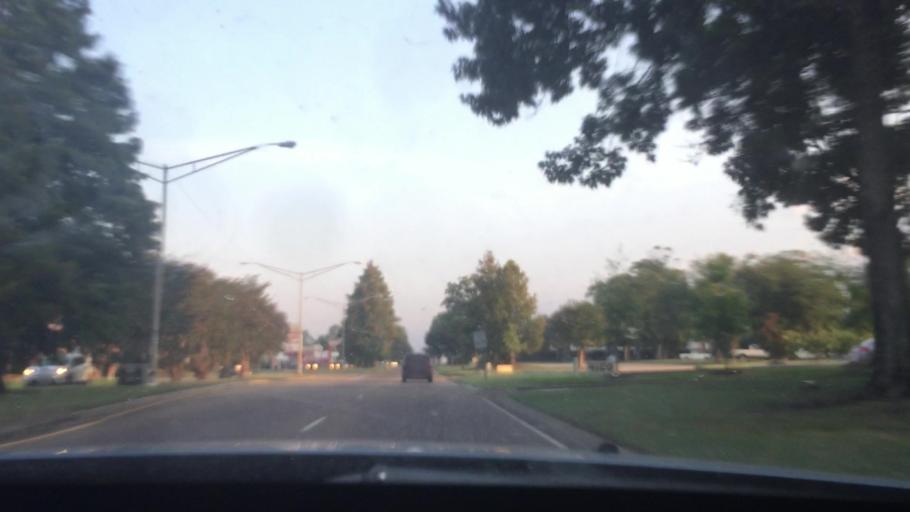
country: US
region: Louisiana
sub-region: East Baton Rouge Parish
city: Inniswold
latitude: 30.4167
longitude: -91.0517
